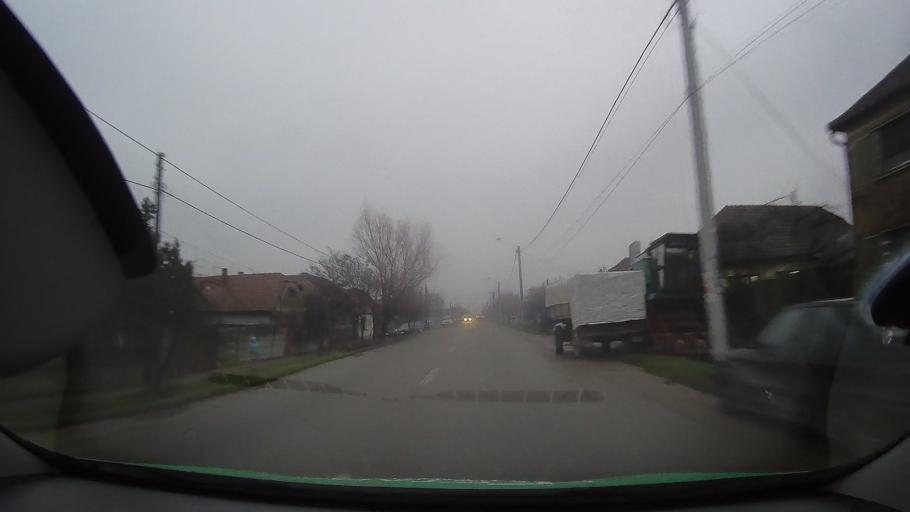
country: RO
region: Bihor
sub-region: Municipiul Salonta
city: Salonta
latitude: 46.7963
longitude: 21.6718
